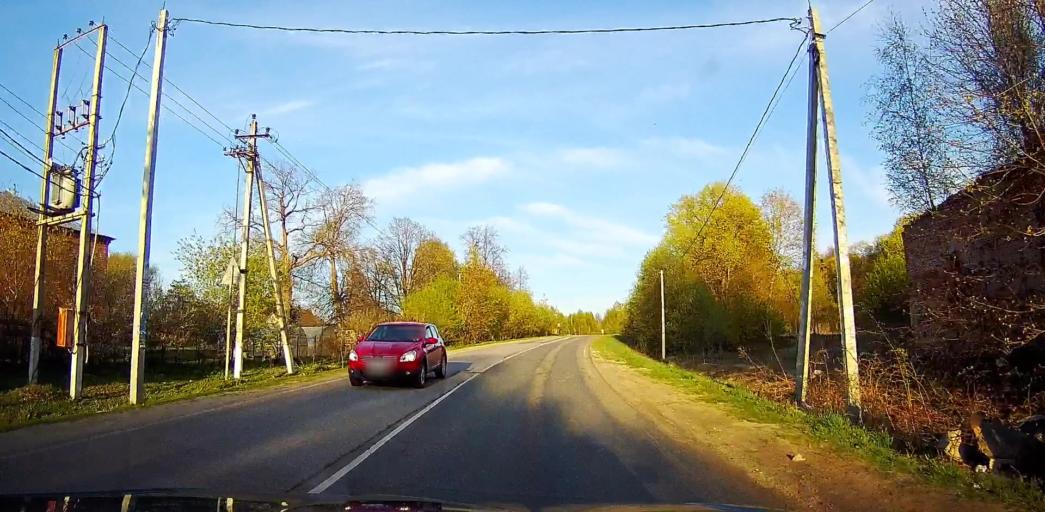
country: RU
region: Moskovskaya
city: Meshcherino
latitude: 55.2528
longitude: 38.2768
